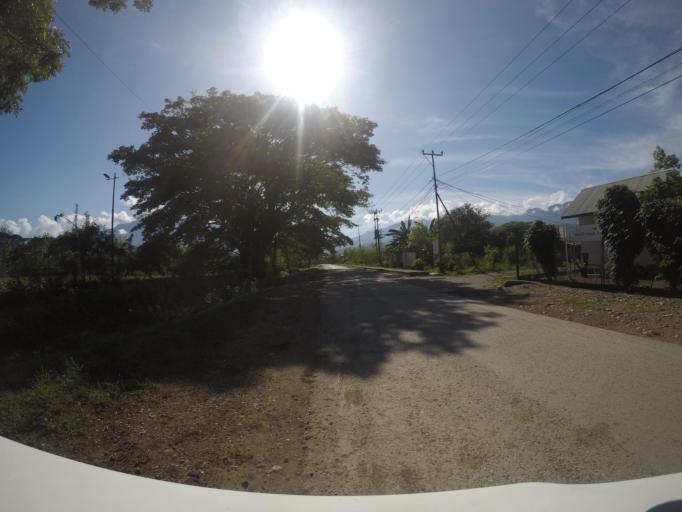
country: TL
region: Bobonaro
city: Maliana
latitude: -8.9925
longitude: 125.1908
